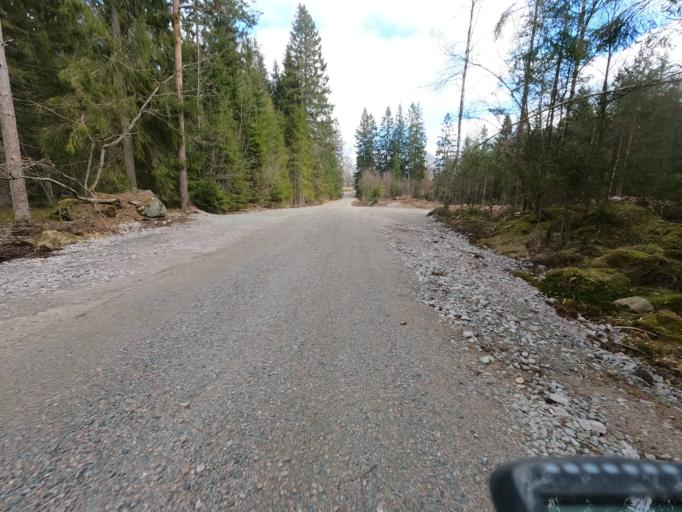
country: SE
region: Kronoberg
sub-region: Alvesta Kommun
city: Vislanda
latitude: 56.8184
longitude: 14.3571
